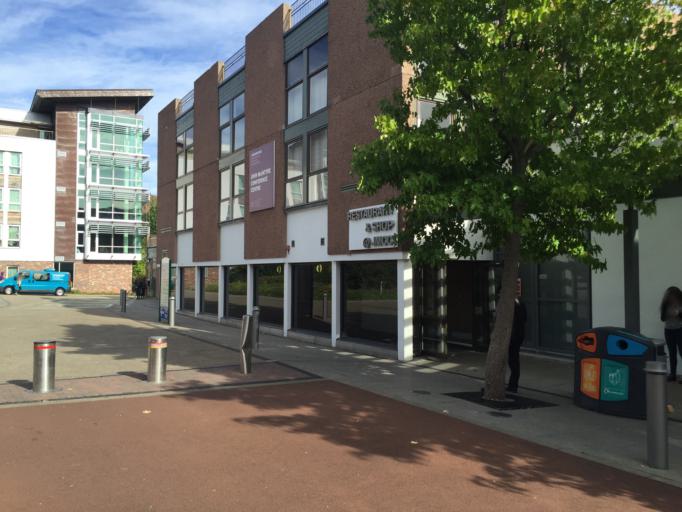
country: GB
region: Scotland
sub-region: Edinburgh
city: Edinburgh
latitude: 55.9398
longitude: -3.1701
